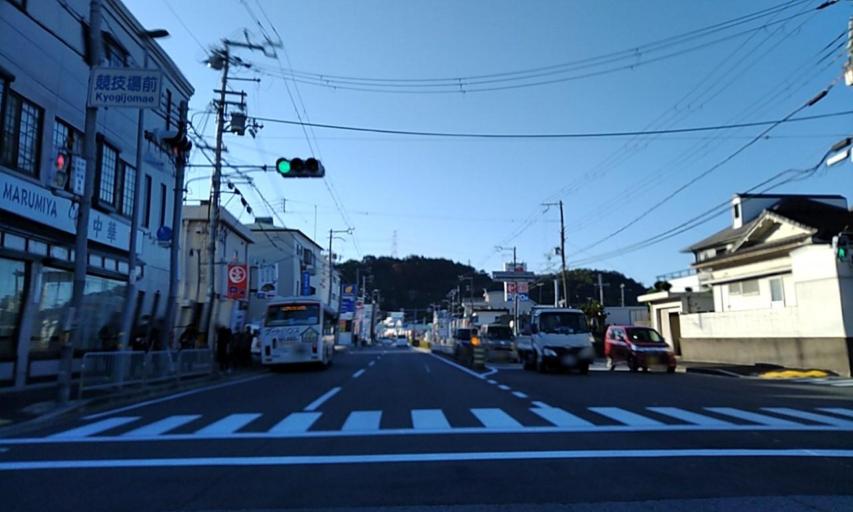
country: JP
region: Wakayama
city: Kainan
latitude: 34.1664
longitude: 135.1873
